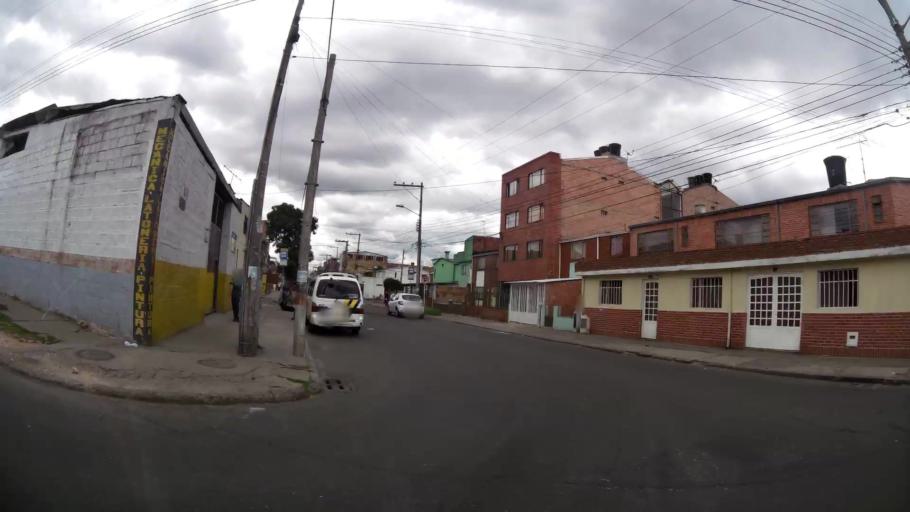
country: CO
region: Bogota D.C.
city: Bogota
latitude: 4.6144
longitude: -74.1198
